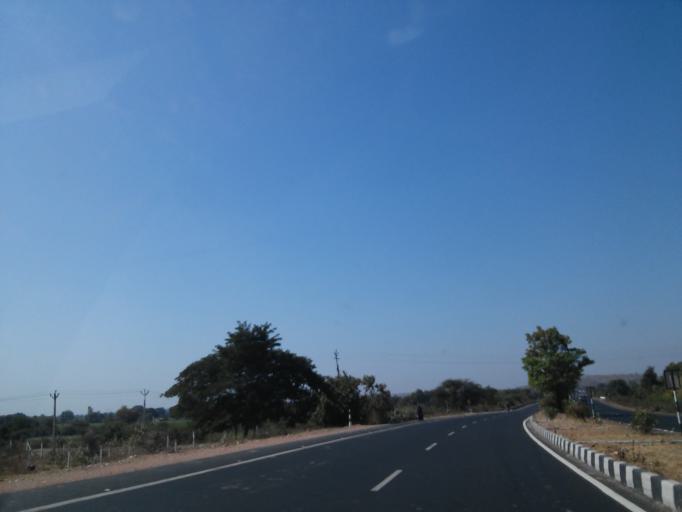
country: IN
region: Gujarat
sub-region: Sabar Kantha
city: Modasa
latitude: 23.5986
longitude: 73.2015
